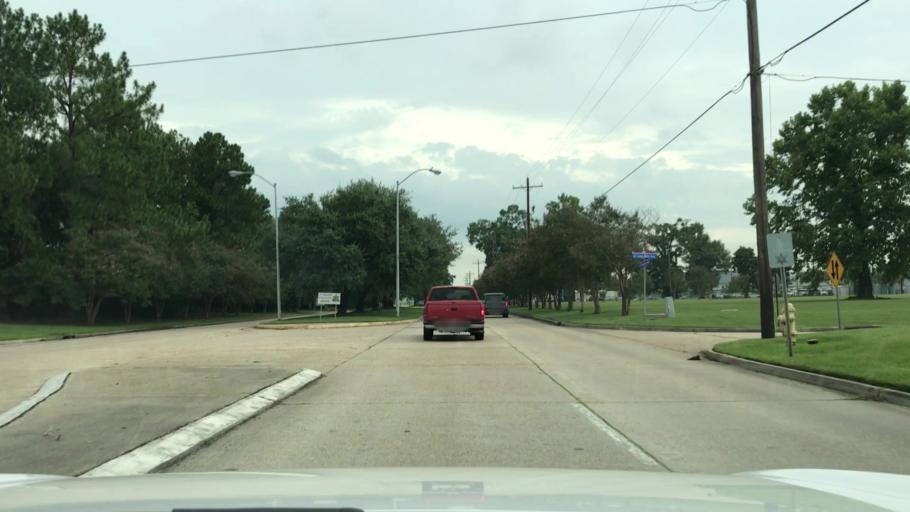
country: US
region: Louisiana
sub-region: East Baton Rouge Parish
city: Brownsfield
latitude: 30.5328
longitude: -91.1612
